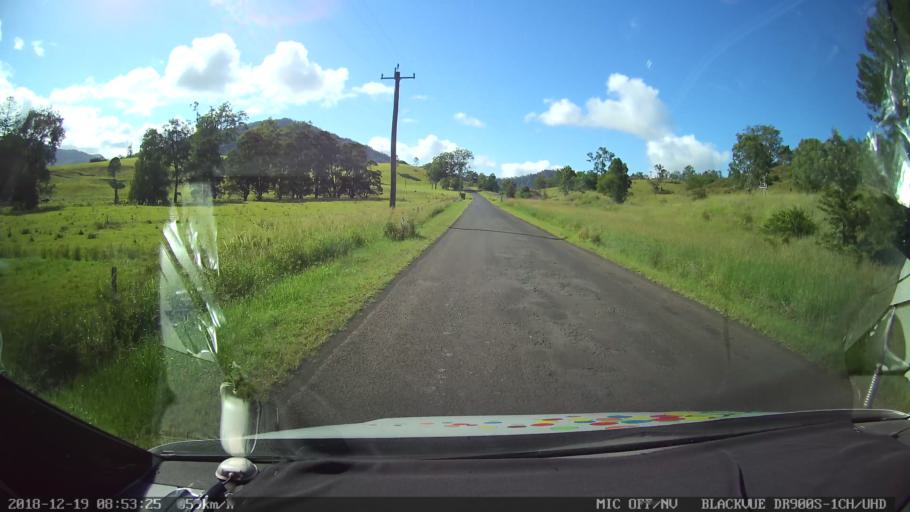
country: AU
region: New South Wales
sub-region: Kyogle
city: Kyogle
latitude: -28.4013
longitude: 152.9771
